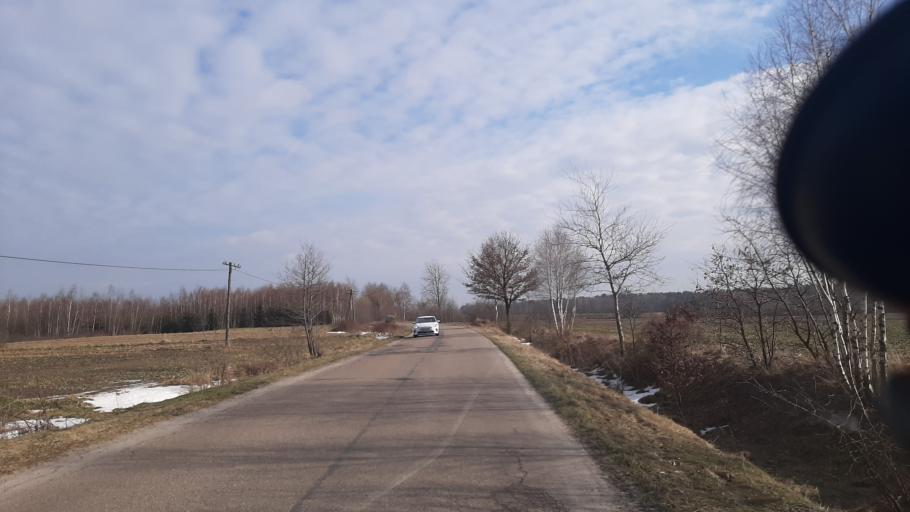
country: PL
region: Lublin Voivodeship
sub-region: Powiat lubartowski
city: Uscimow Stary
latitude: 51.4697
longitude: 22.9736
